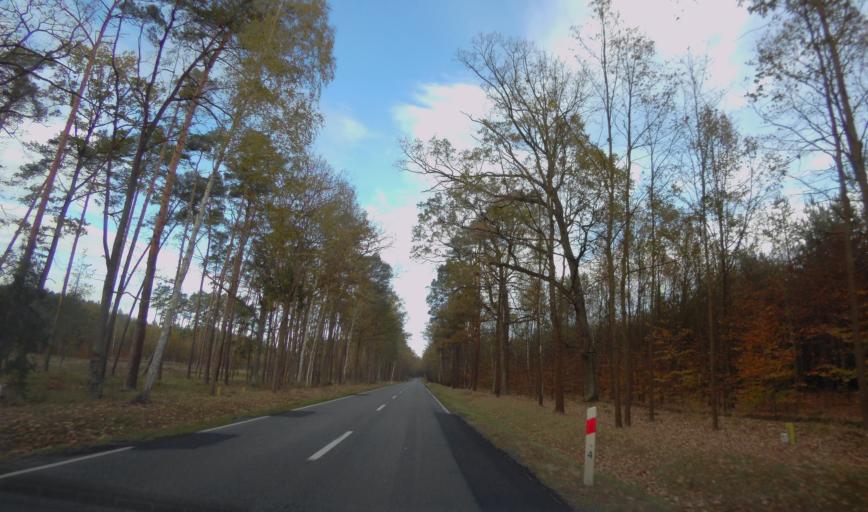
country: PL
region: Subcarpathian Voivodeship
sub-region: Powiat nizanski
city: Krzeszow
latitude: 50.3803
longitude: 22.3100
